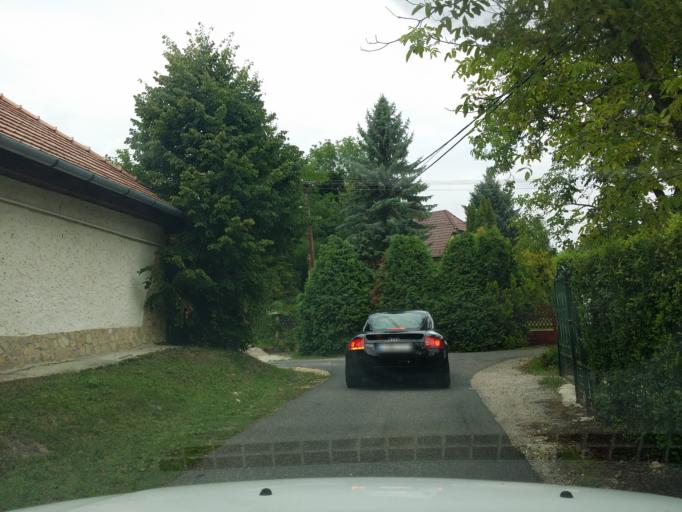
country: HU
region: Borsod-Abauj-Zemplen
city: Gonc
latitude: 48.4860
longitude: 21.3653
